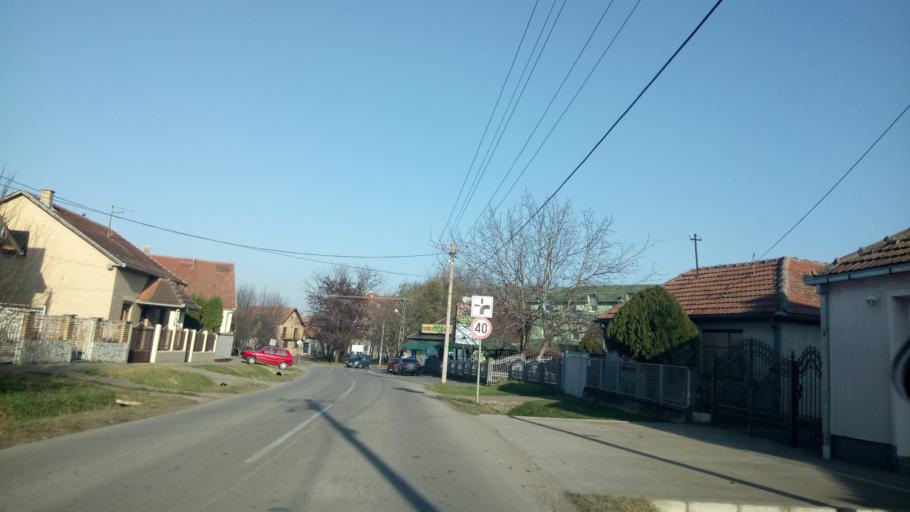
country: RS
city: Beska
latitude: 45.1242
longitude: 20.0644
